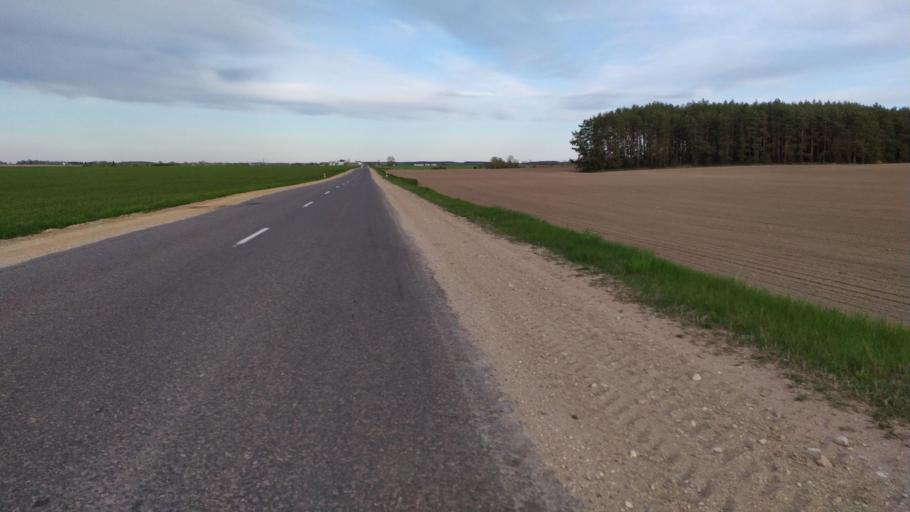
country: BY
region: Brest
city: Kamyanyets
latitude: 52.4073
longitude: 23.7411
